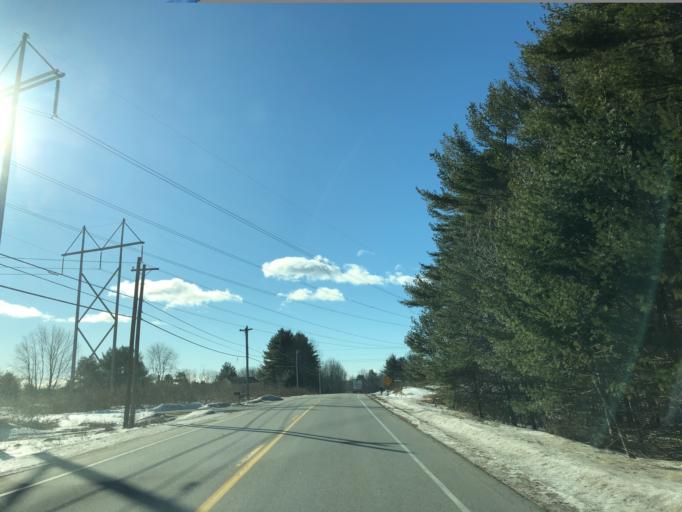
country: US
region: Maine
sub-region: Cumberland County
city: South Windham
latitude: 43.7534
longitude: -70.4248
